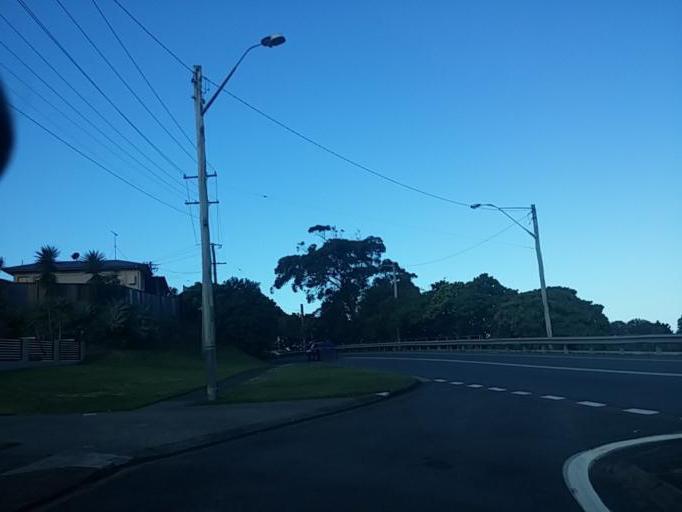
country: AU
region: New South Wales
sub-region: Tweed
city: Tweed Heads West
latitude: -28.1849
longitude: 153.5341
